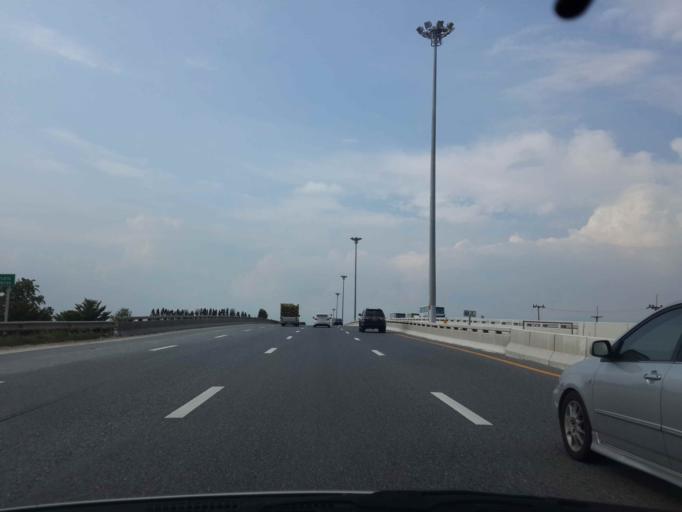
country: TH
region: Chon Buri
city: Phan Thong
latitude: 13.4791
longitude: 101.0462
